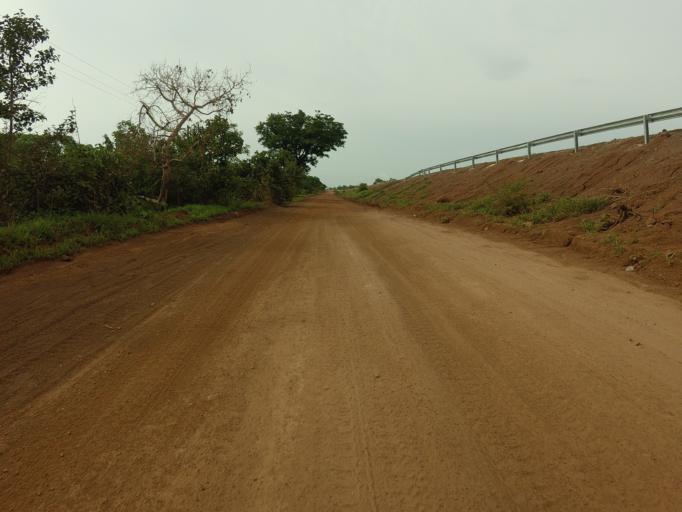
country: GH
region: Northern
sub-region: Yendi
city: Yendi
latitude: 9.6545
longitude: -0.0718
